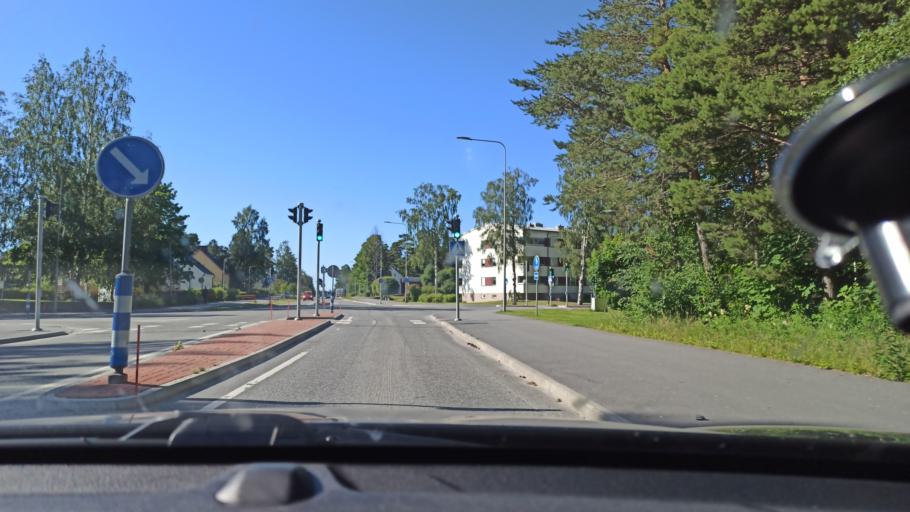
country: FI
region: Ostrobothnia
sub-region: Jakobstadsregionen
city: Jakobstad
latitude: 63.6806
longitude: 22.7172
